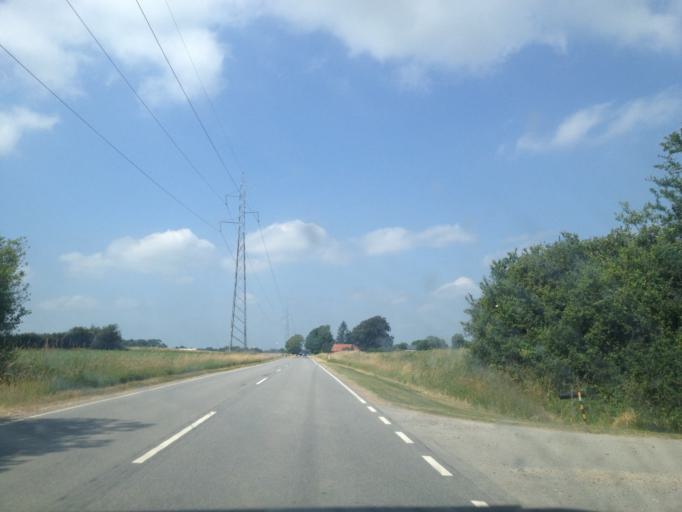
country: DK
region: South Denmark
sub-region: Kolding Kommune
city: Vamdrup
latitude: 55.3623
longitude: 9.2847
